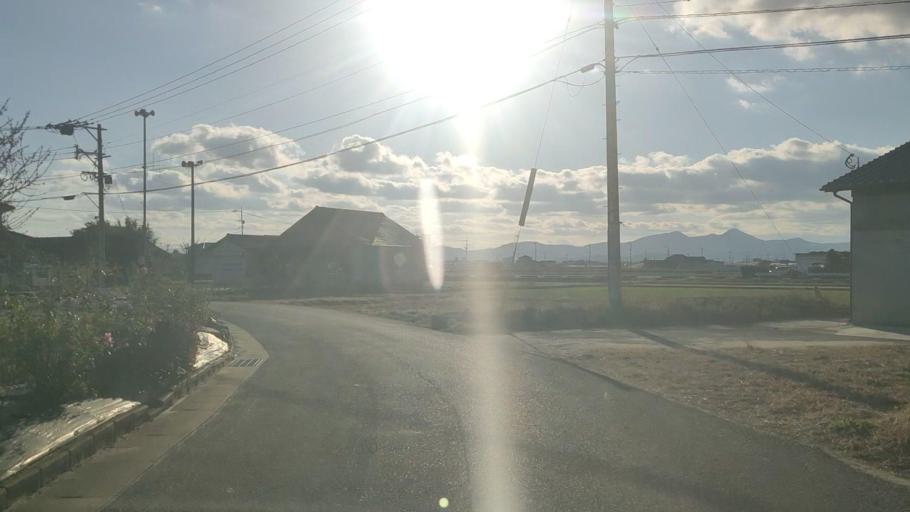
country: JP
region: Saga Prefecture
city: Saga-shi
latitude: 33.2936
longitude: 130.2406
